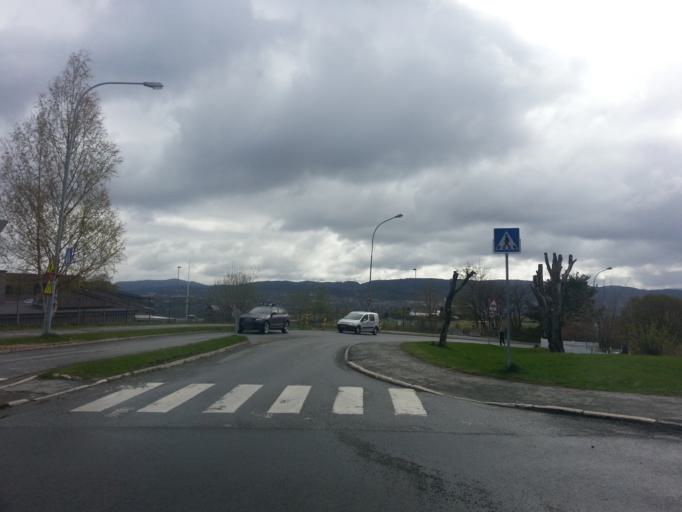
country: NO
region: Sor-Trondelag
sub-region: Trondheim
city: Trondheim
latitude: 63.4100
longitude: 10.3506
